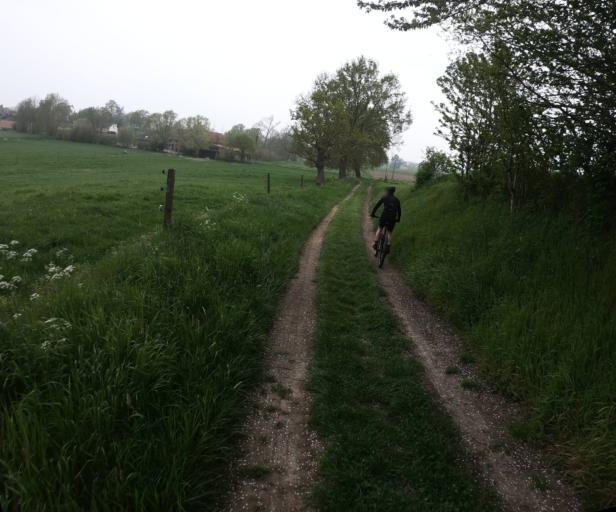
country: BE
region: Flanders
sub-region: Provincie Vlaams-Brabant
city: Pepingen
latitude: 50.7371
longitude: 4.1543
